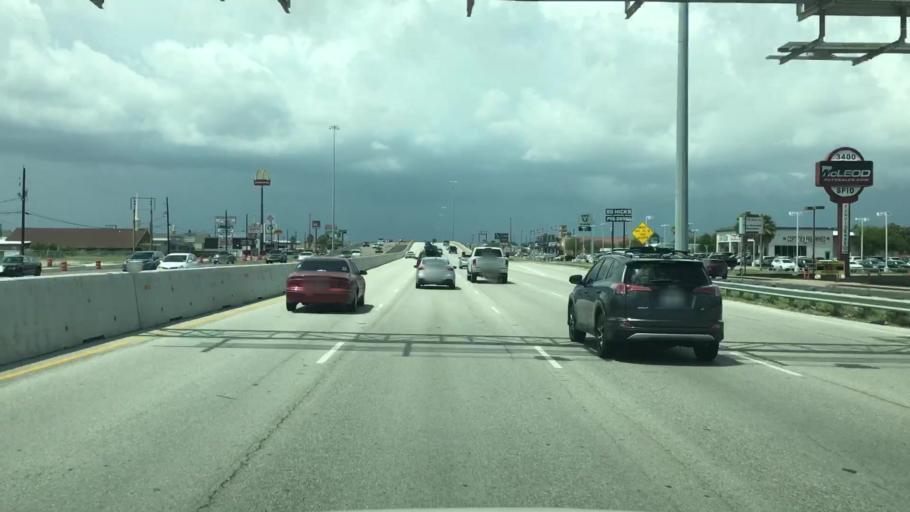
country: US
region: Texas
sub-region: Nueces County
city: Corpus Christi
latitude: 27.7267
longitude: -97.4088
